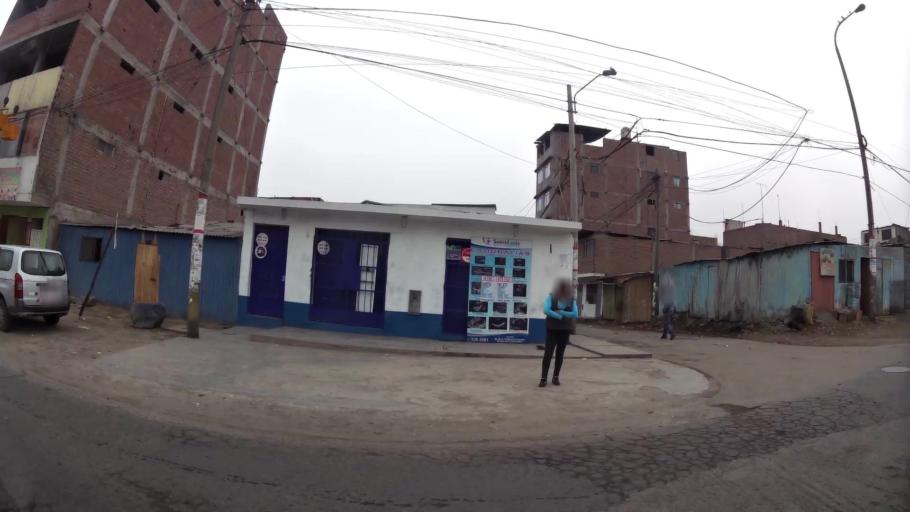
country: PE
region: Lima
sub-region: Lima
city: Independencia
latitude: -11.9458
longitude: -76.9778
